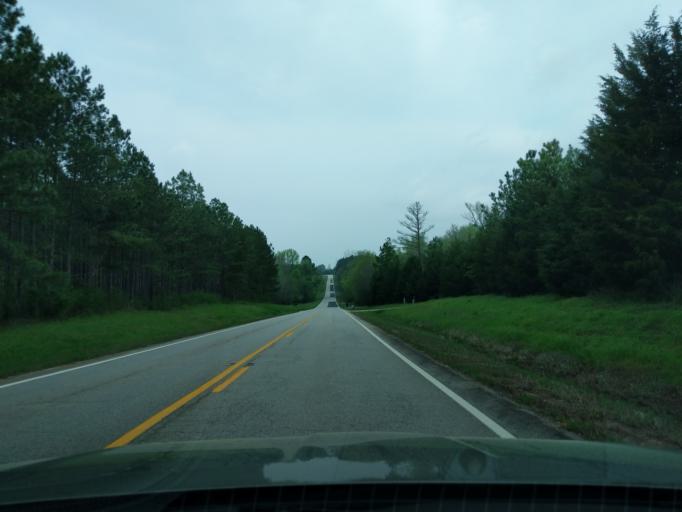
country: US
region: Georgia
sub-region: Lincoln County
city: Lincolnton
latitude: 33.7946
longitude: -82.3850
